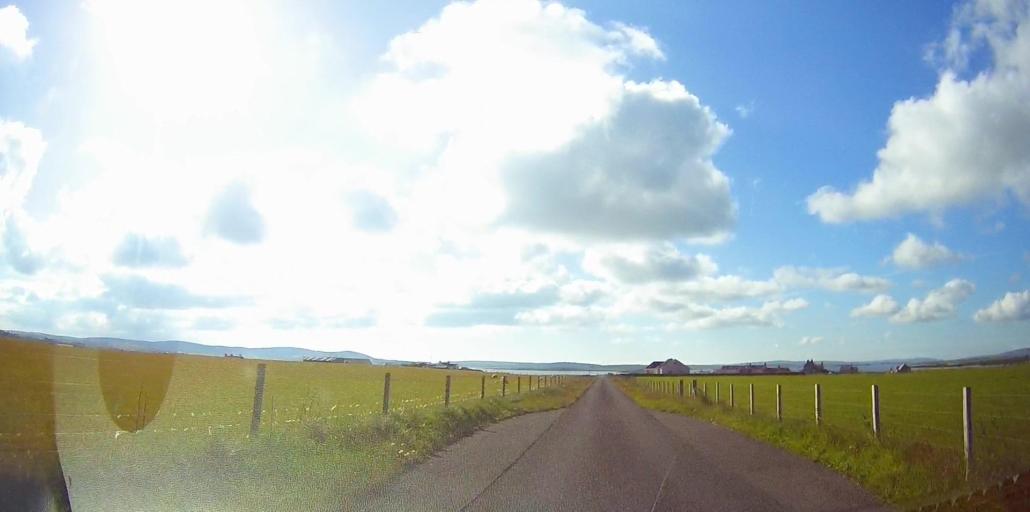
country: GB
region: Scotland
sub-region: Orkney Islands
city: Stromness
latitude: 58.9868
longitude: -3.1935
